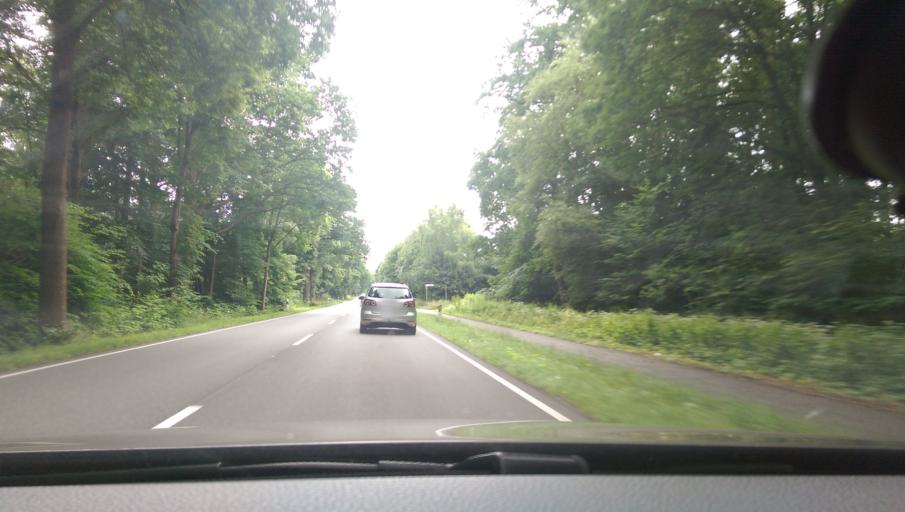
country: DE
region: Lower Saxony
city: Botersen
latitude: 53.1508
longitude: 9.3325
